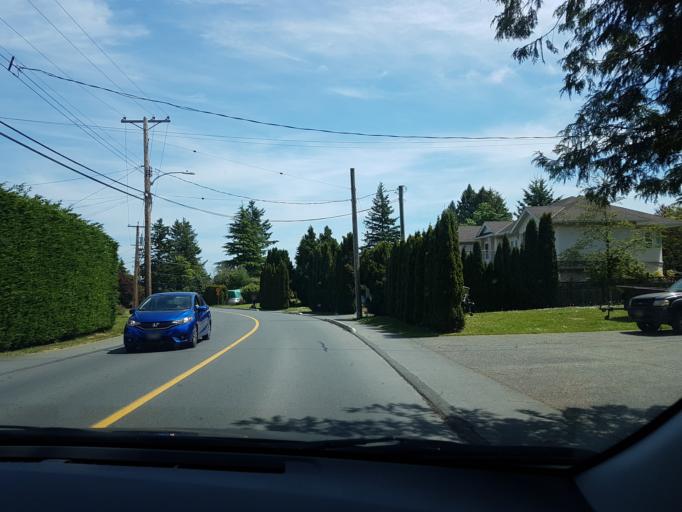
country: CA
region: British Columbia
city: Oak Bay
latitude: 48.4885
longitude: -123.3150
